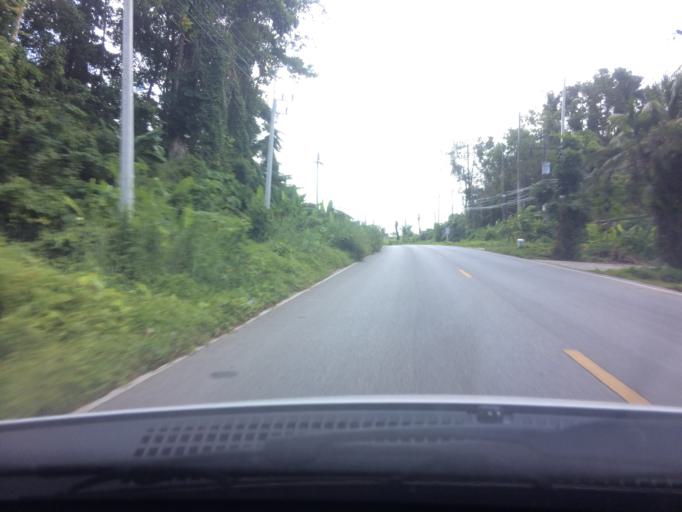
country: TH
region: Phuket
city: Thalang
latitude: 8.0891
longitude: 98.3638
